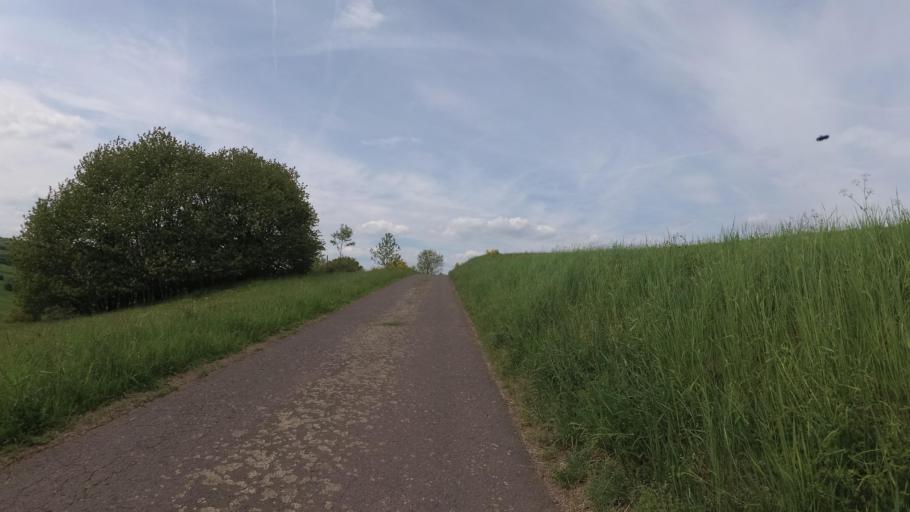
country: DE
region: Rheinland-Pfalz
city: Eckersweiler
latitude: 49.5622
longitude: 7.2962
